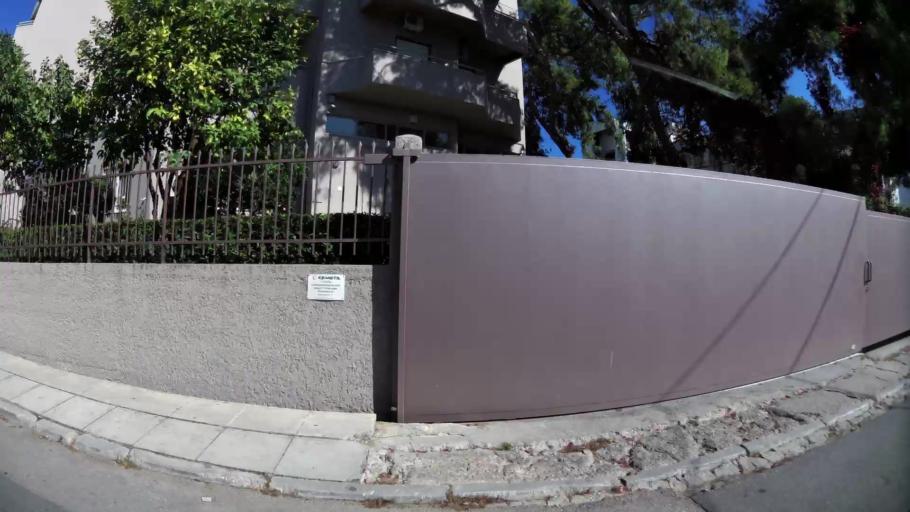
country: GR
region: Attica
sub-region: Nomarchia Athinas
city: Metamorfosi
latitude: 38.0679
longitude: 23.7650
